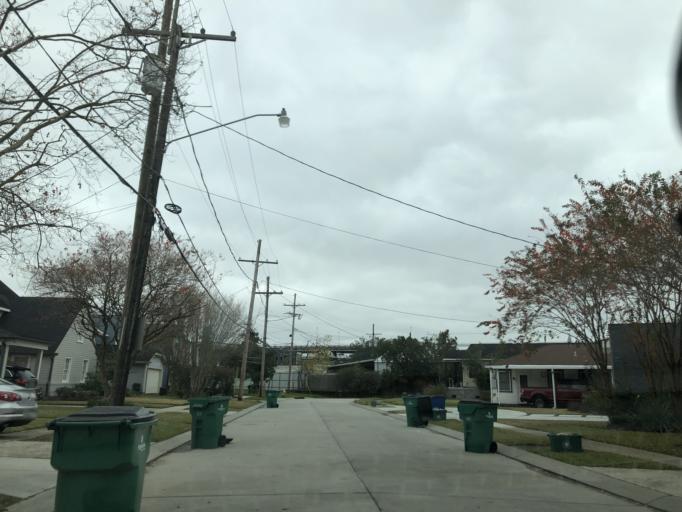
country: US
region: Louisiana
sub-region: Jefferson Parish
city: Metairie
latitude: 29.9760
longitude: -90.1540
